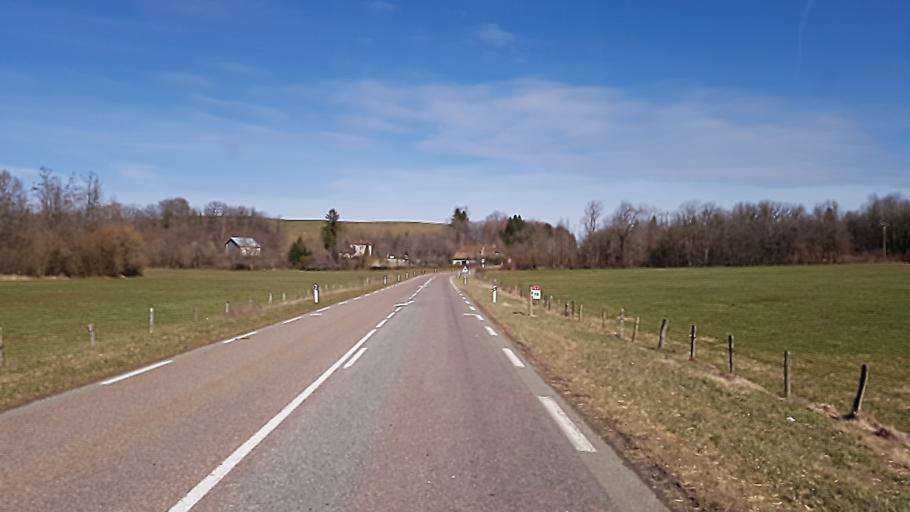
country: FR
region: Franche-Comte
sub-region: Departement du Jura
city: Champagnole
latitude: 46.6812
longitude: 5.9314
